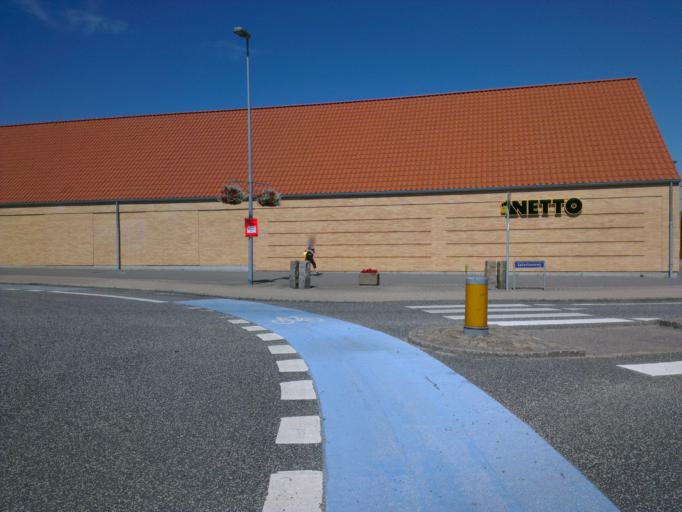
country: DK
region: Capital Region
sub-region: Frederikssund Kommune
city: Slangerup
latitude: 55.8428
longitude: 12.1751
